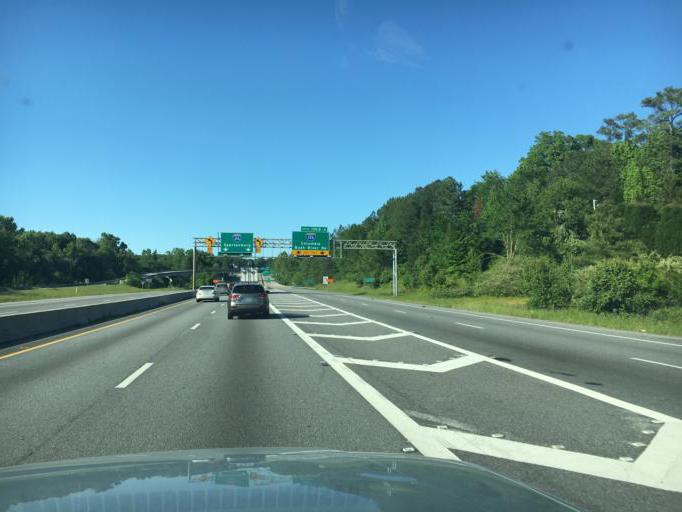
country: US
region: South Carolina
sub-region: Lexington County
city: Saint Andrews
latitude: 34.0209
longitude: -81.1048
